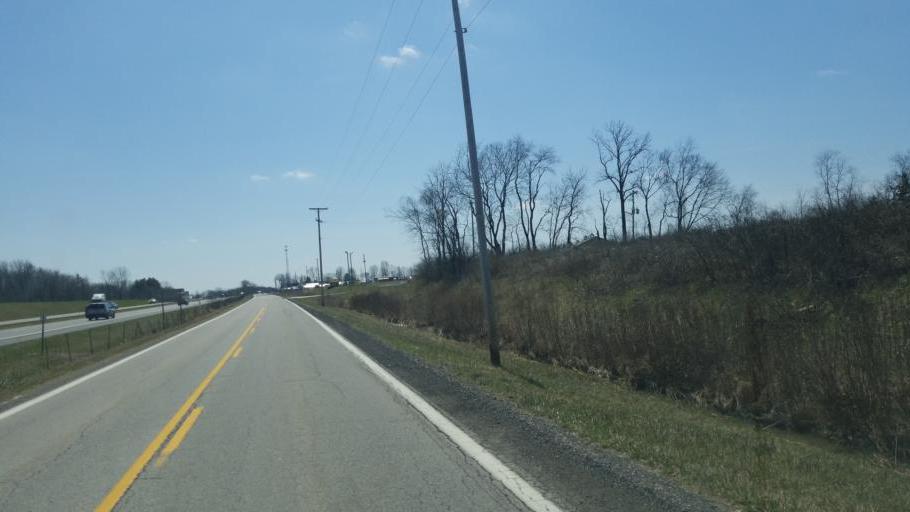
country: US
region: Ohio
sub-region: Marion County
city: Prospect
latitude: 40.4503
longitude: -83.0754
